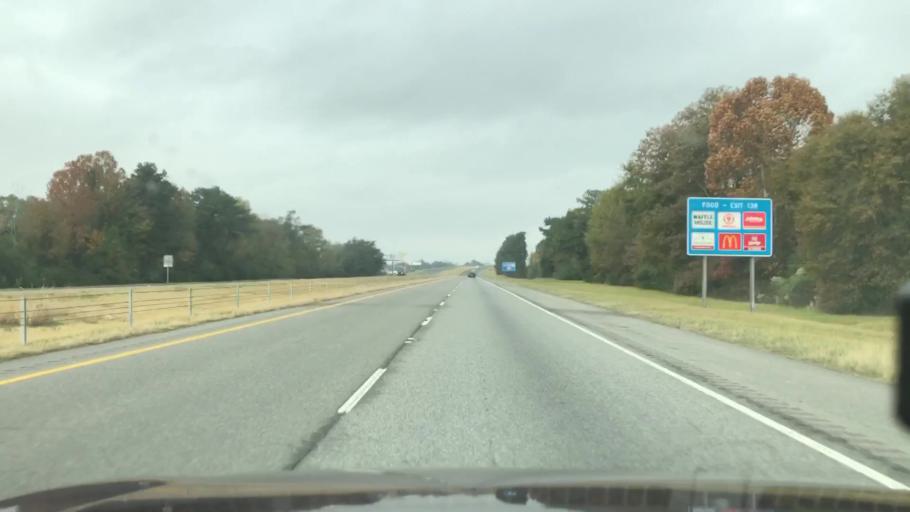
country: US
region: Louisiana
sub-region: Richland Parish
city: Rayville
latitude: 32.4567
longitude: -91.7491
